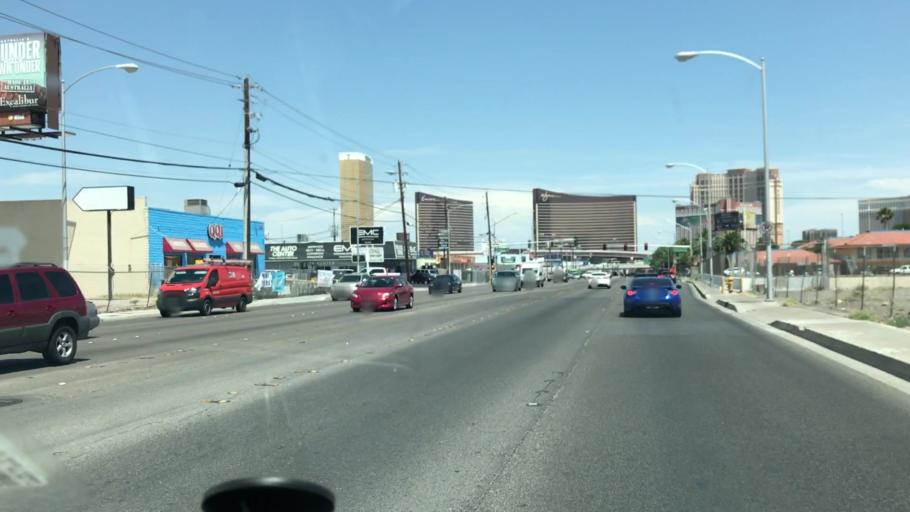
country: US
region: Nevada
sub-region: Clark County
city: Paradise
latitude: 36.1255
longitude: -115.1875
